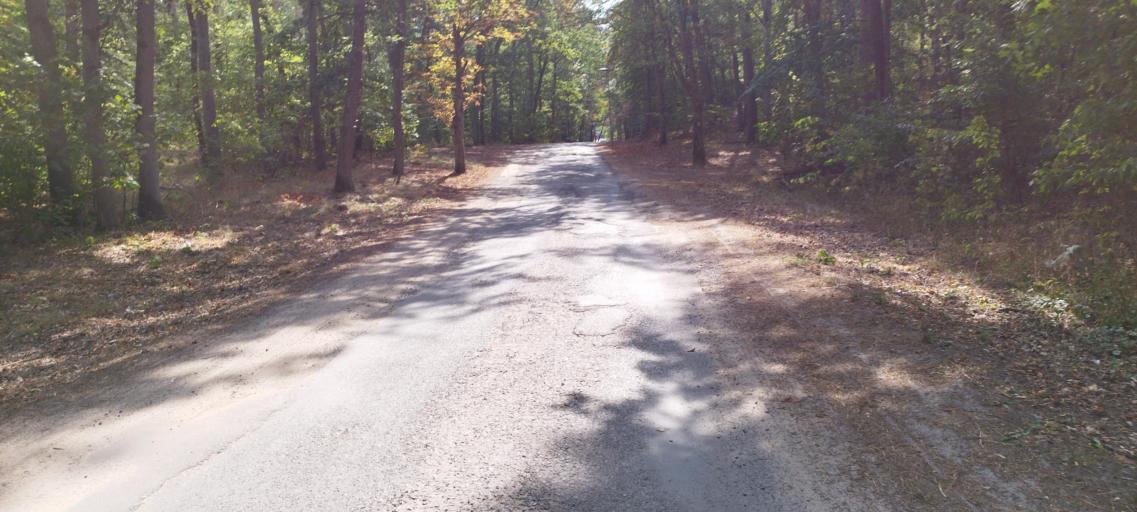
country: DE
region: Brandenburg
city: Strausberg
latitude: 52.5600
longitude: 13.8887
